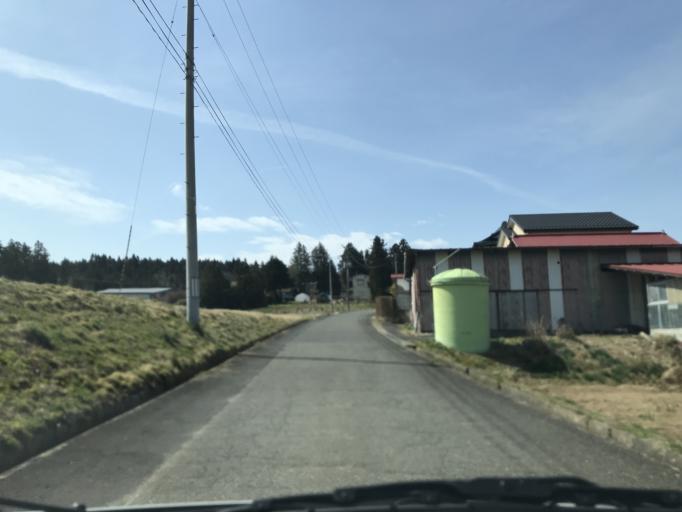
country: JP
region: Iwate
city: Ichinoseki
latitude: 38.8447
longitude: 141.1060
